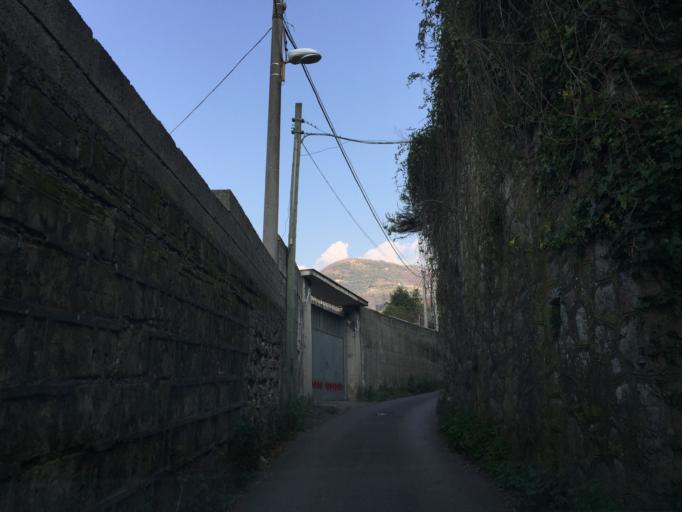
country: IT
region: Campania
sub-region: Provincia di Napoli
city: Castellammare di Stabia
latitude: 40.6868
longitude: 14.4858
